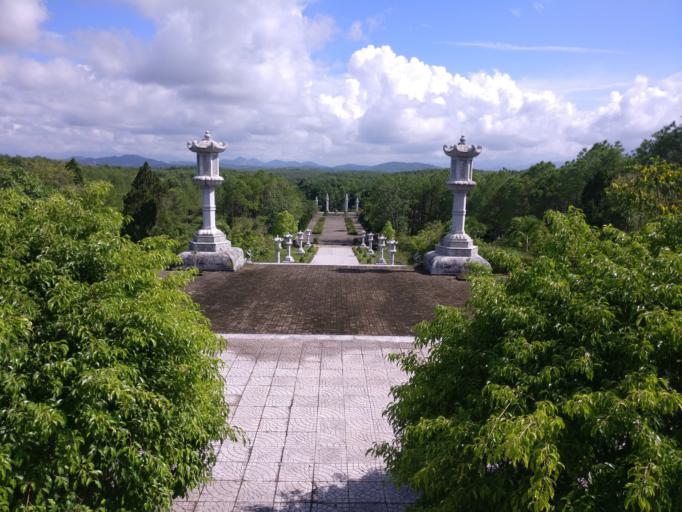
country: VN
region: Thua Thien-Hue
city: Hue
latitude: 16.4208
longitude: 107.6089
